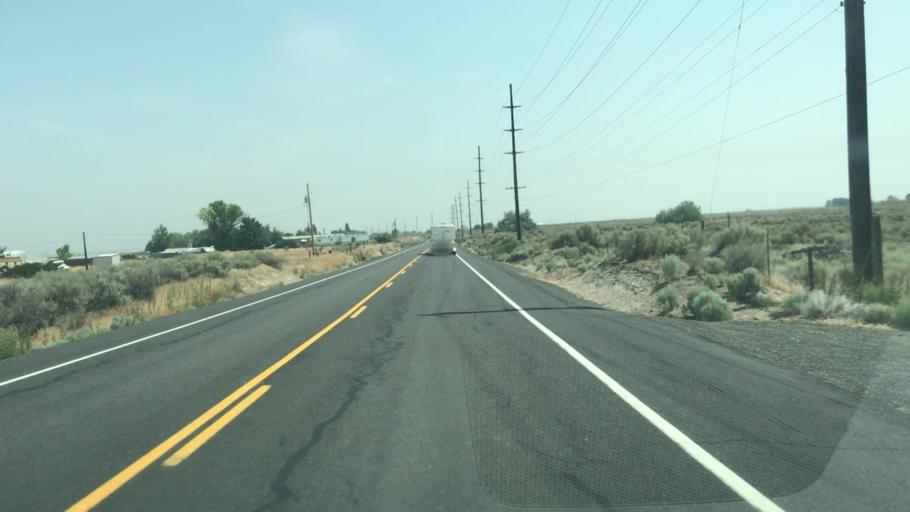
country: US
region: Washington
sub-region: Grant County
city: Quincy
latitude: 47.1601
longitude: -119.8950
